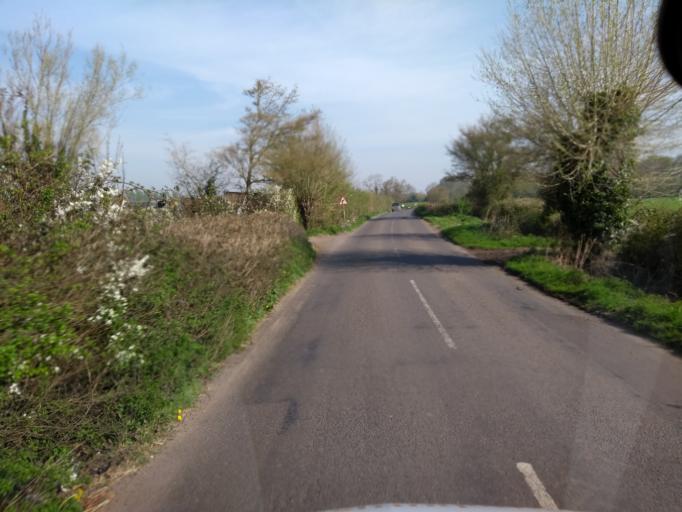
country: GB
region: England
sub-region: Somerset
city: Creech Saint Michael
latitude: 51.0172
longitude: -3.0426
